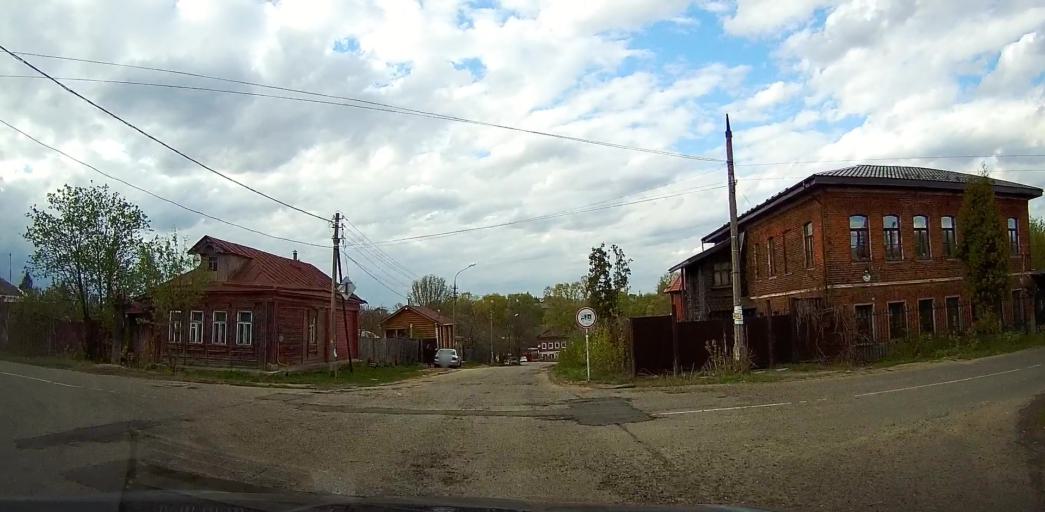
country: RU
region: Moskovskaya
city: Pavlovskiy Posad
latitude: 55.7815
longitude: 38.6559
